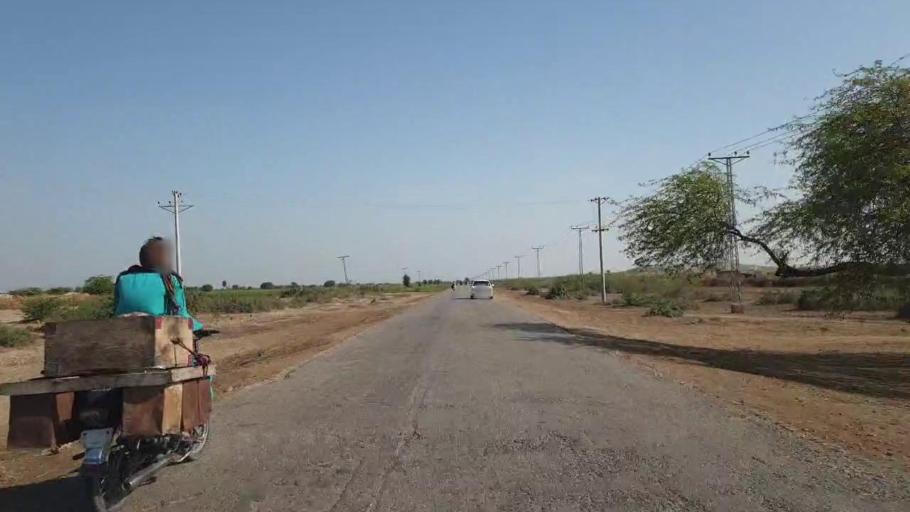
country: PK
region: Sindh
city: Umarkot
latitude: 25.4214
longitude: 69.7361
